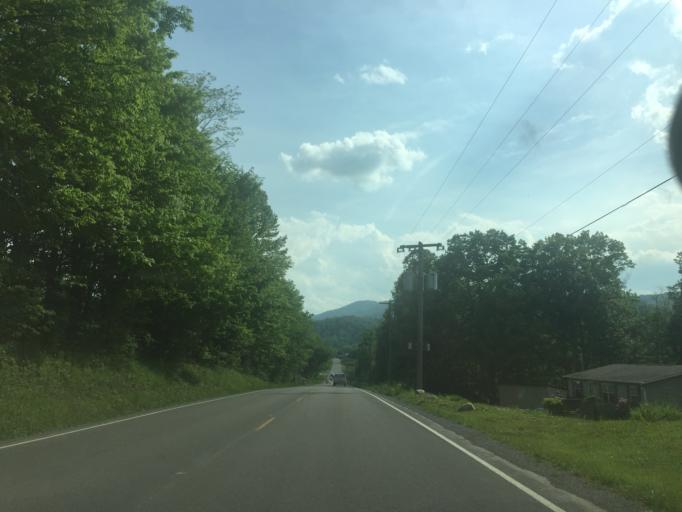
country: US
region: West Virginia
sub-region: Tucker County
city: Parsons
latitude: 38.9722
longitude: -79.4986
